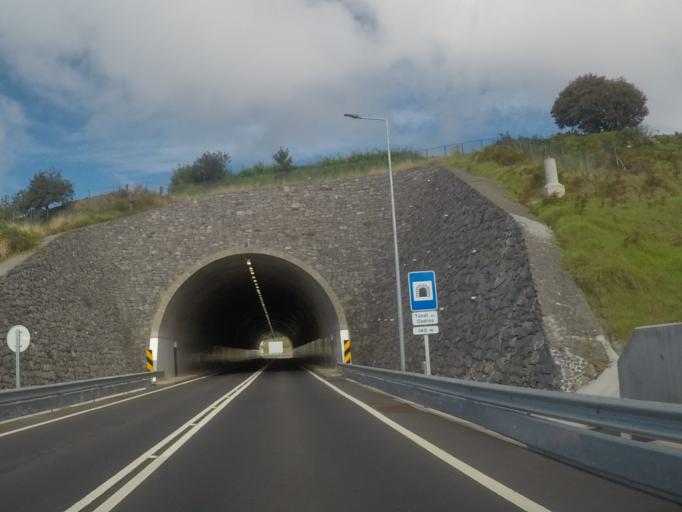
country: PT
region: Madeira
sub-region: Calheta
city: Faja da Ovelha
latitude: 32.7717
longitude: -17.2178
